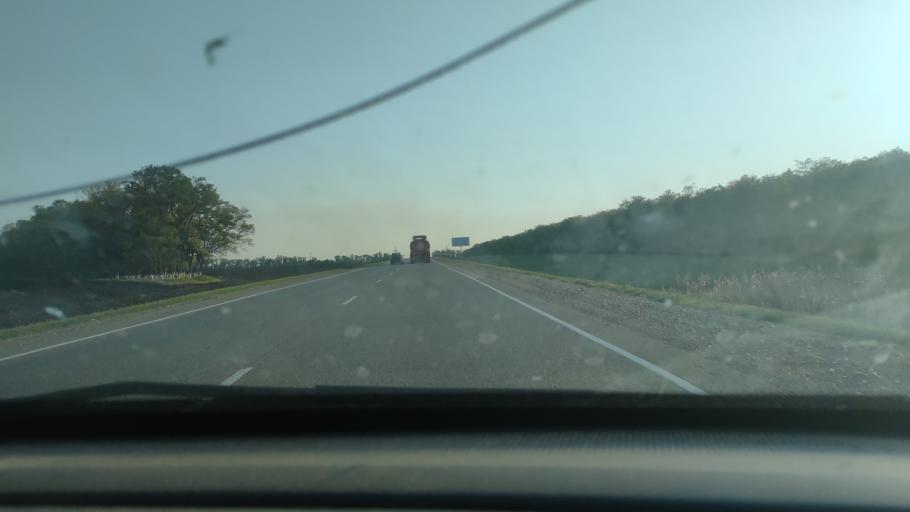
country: RU
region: Krasnodarskiy
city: Kanevskaya
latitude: 46.0386
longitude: 38.9838
